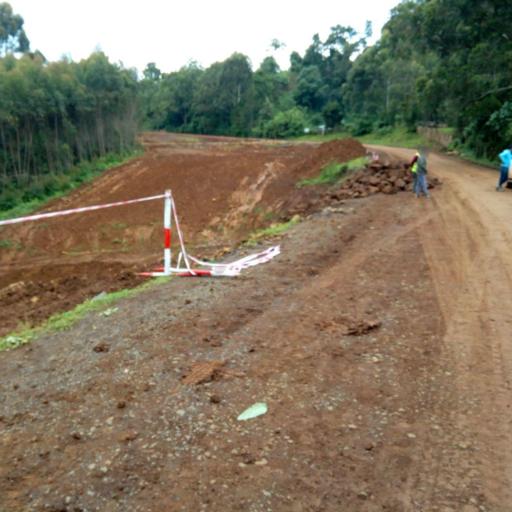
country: ET
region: Oromiya
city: Gore
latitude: 7.7208
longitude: 35.4834
